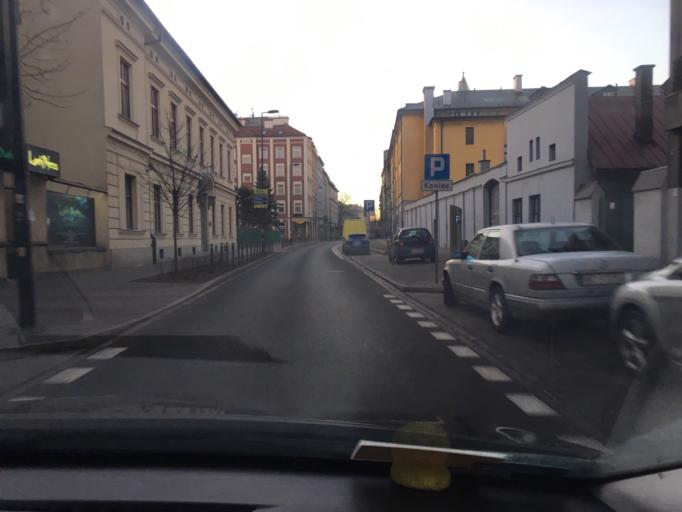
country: PL
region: Lesser Poland Voivodeship
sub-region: Krakow
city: Krakow
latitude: 50.0696
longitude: 19.9436
